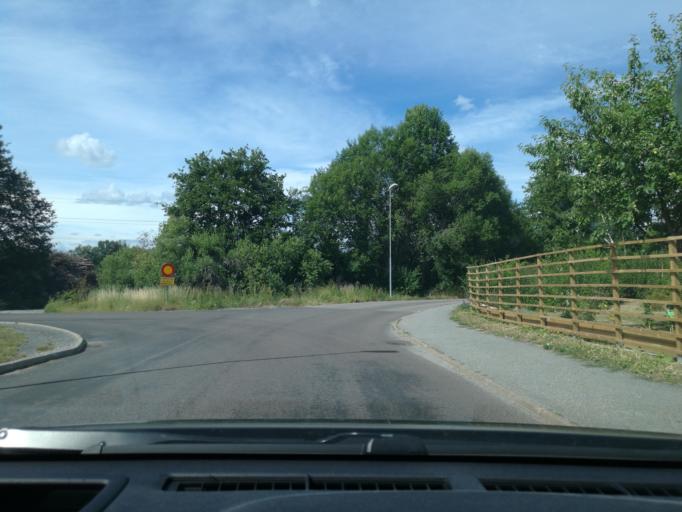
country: SE
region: Stockholm
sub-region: Upplands Vasby Kommun
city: Upplands Vaesby
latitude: 59.4851
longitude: 17.8922
